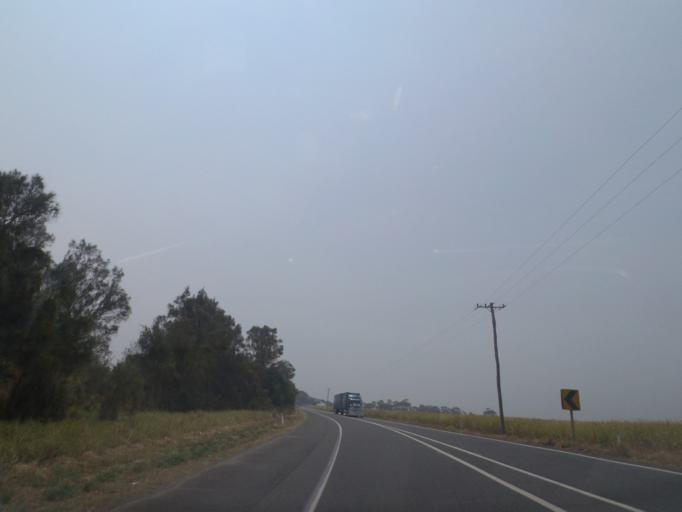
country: AU
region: New South Wales
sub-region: Richmond Valley
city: Evans Head
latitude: -28.9920
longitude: 153.4622
